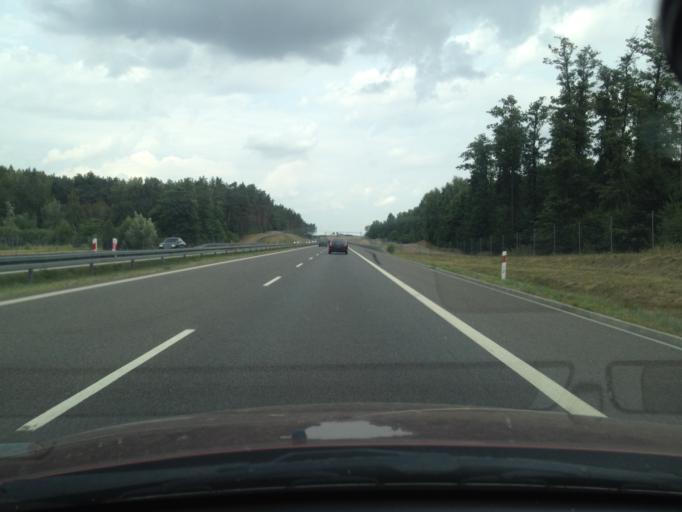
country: PL
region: West Pomeranian Voivodeship
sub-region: Powiat mysliborski
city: Mysliborz
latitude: 53.0124
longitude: 14.8619
